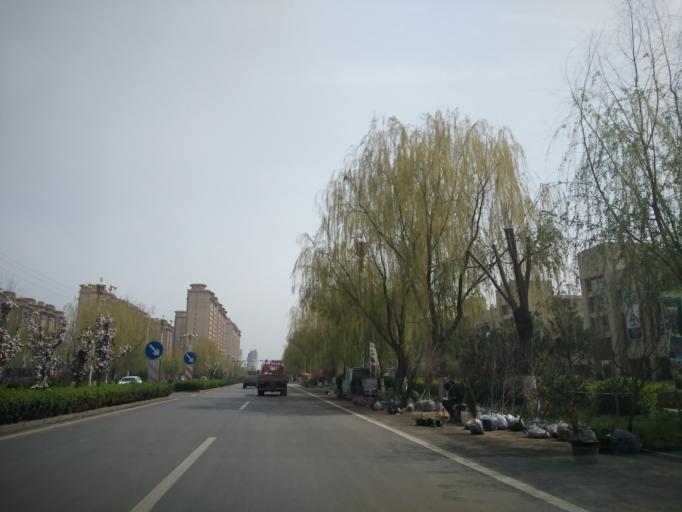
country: CN
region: Beijing
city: Xiji
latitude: 39.7455
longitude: 116.9788
